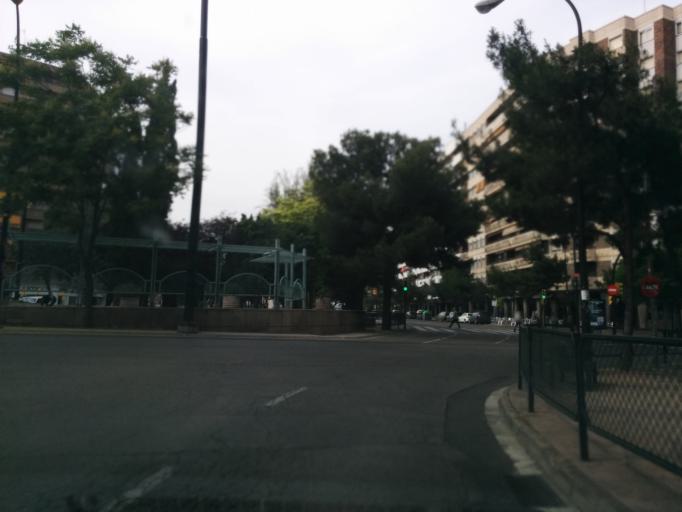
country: ES
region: Aragon
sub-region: Provincia de Zaragoza
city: Delicias
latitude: 41.6475
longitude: -0.8937
